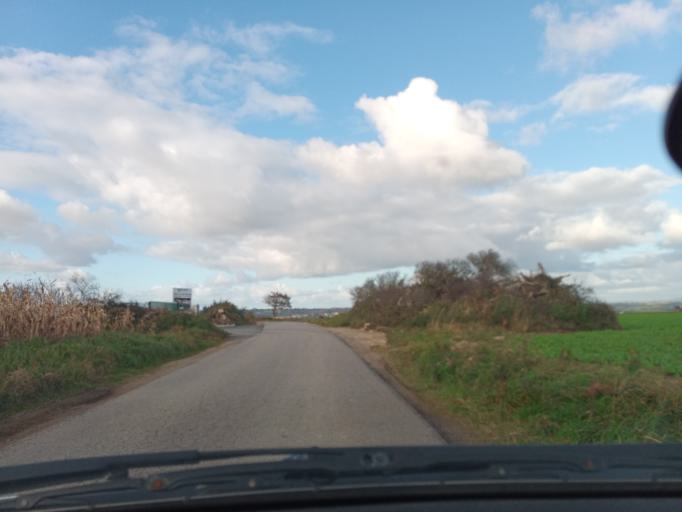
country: FR
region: Brittany
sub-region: Departement du Finistere
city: Plouhinec
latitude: 48.0241
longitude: -4.4981
